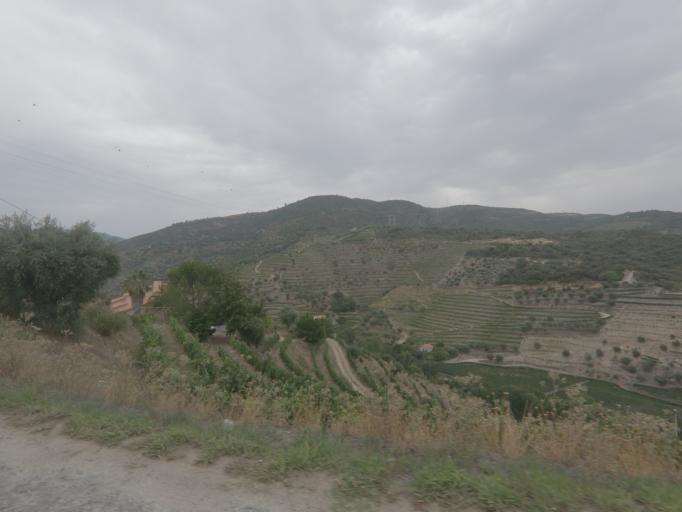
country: PT
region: Viseu
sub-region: Armamar
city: Armamar
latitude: 41.1399
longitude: -7.6429
